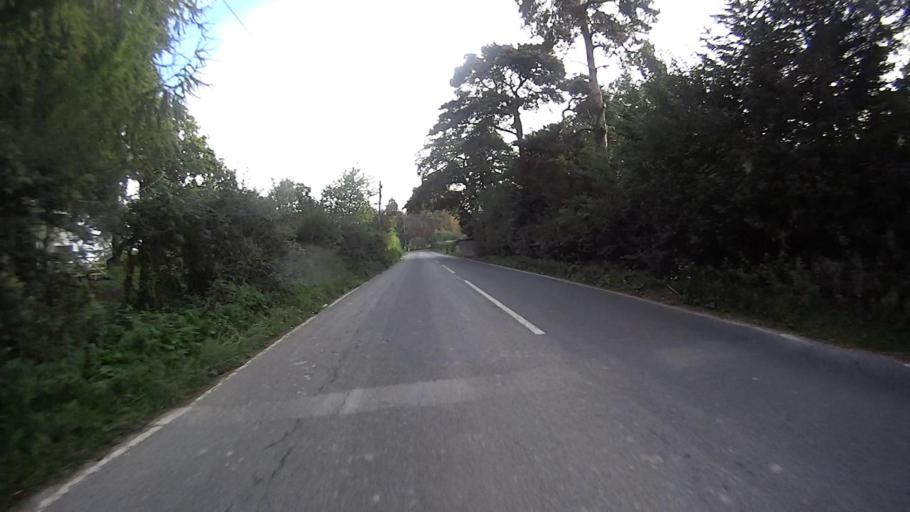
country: GB
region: England
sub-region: West Sussex
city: Copthorne
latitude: 51.1448
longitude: -0.1114
